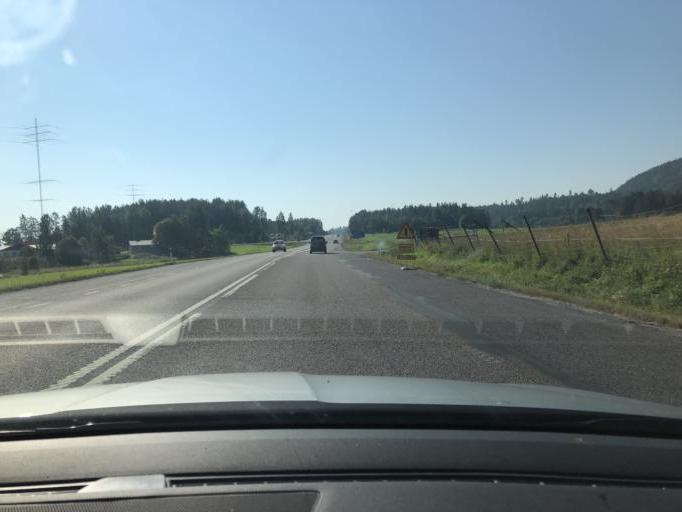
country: SE
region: Vaesternorrland
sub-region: Kramfors Kommun
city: Kramfors
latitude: 62.8771
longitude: 17.8550
